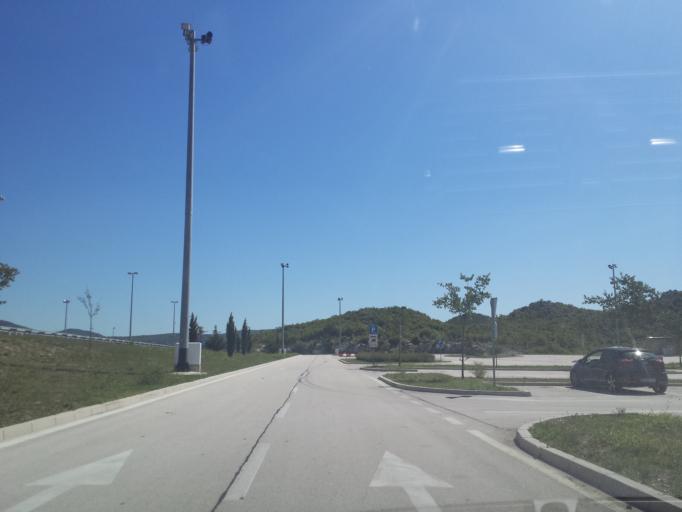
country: HR
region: Splitsko-Dalmatinska
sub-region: Grad Omis
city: Omis
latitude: 43.4927
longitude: 16.7833
